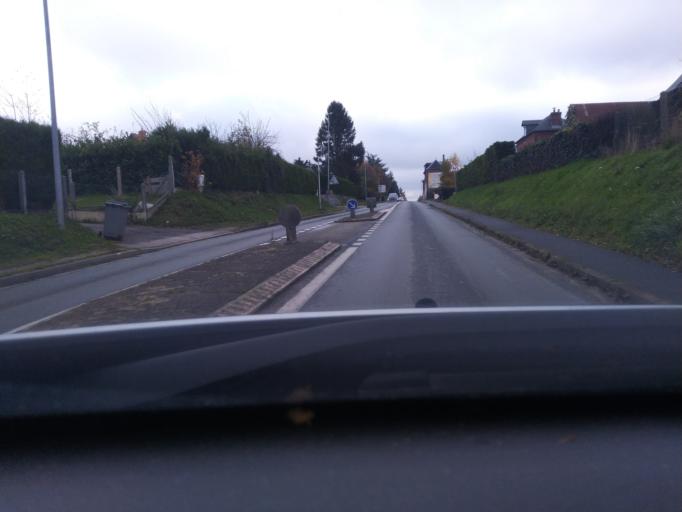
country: FR
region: Haute-Normandie
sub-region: Departement de la Seine-Maritime
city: La Vaupaliere
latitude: 49.4901
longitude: 1.0012
